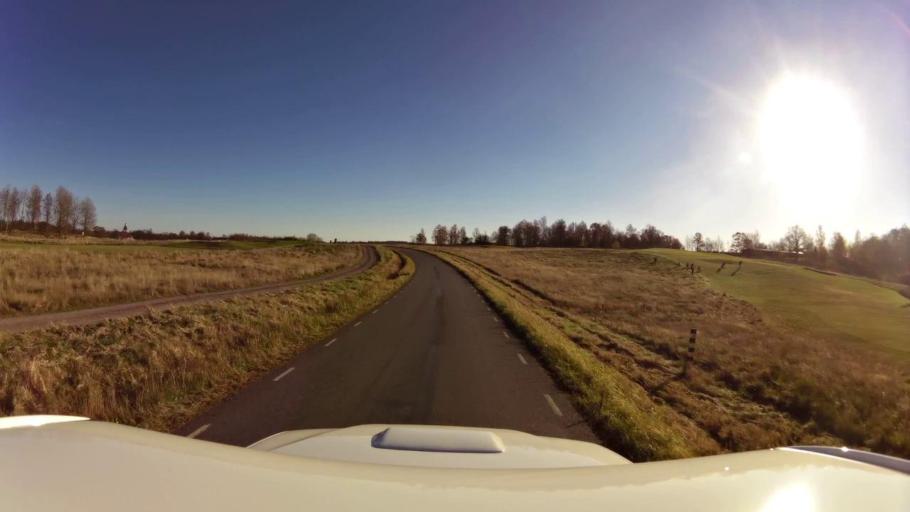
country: SE
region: OEstergoetland
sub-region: Kinda Kommun
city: Rimforsa
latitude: 58.2396
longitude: 15.6744
